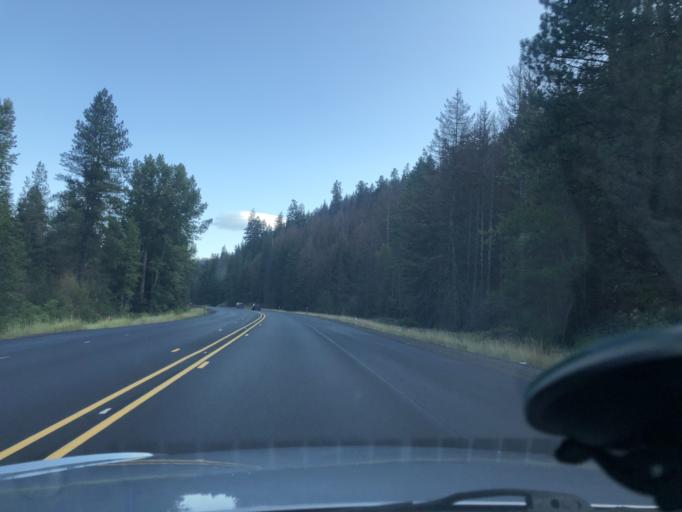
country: US
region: Washington
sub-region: Kittitas County
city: Cle Elum
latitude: 47.2770
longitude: -120.6984
